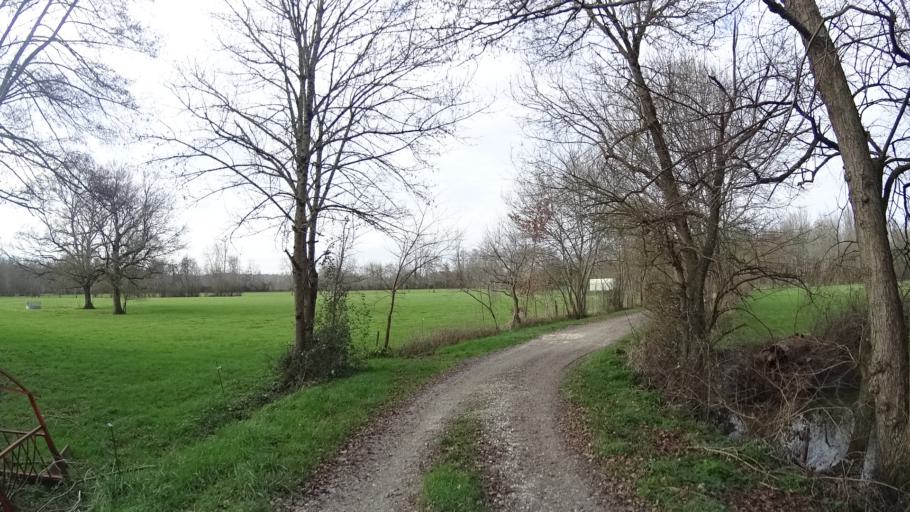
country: FR
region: Aquitaine
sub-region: Departement de la Dordogne
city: Saint-Aulaye
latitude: 45.2109
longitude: 0.1396
